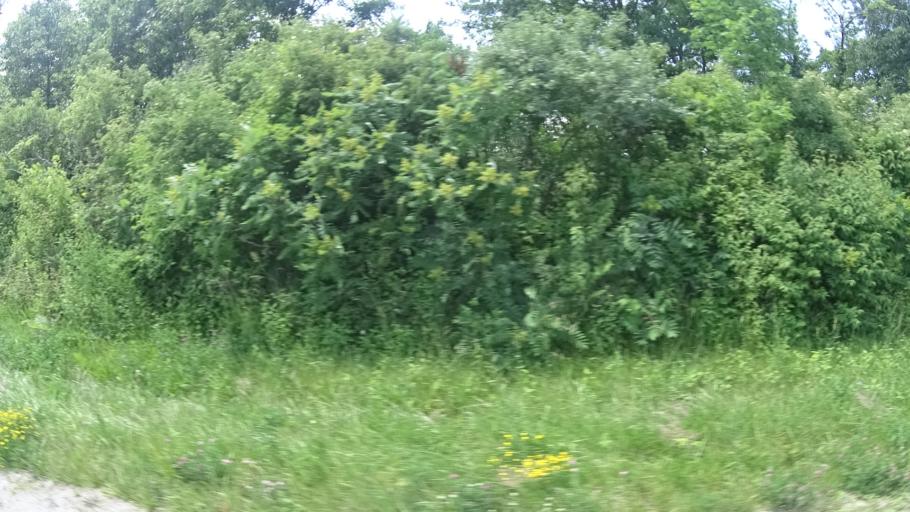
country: US
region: Ohio
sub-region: Erie County
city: Huron
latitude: 41.3658
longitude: -82.5467
